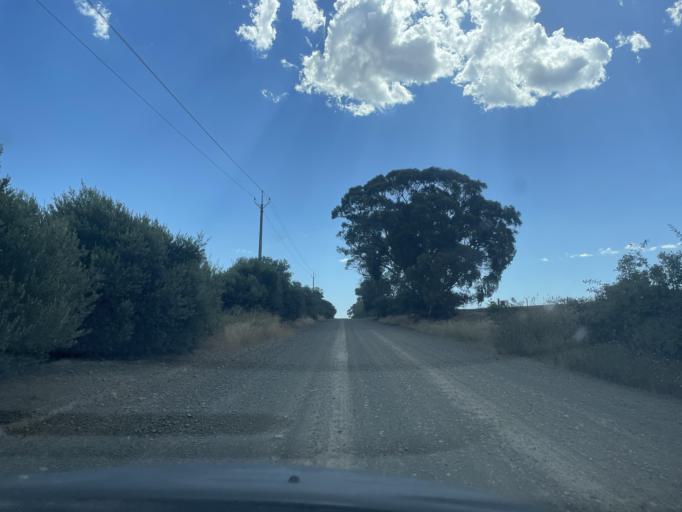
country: AU
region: South Australia
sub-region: Clare and Gilbert Valleys
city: Clare
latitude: -33.9095
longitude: 138.7331
